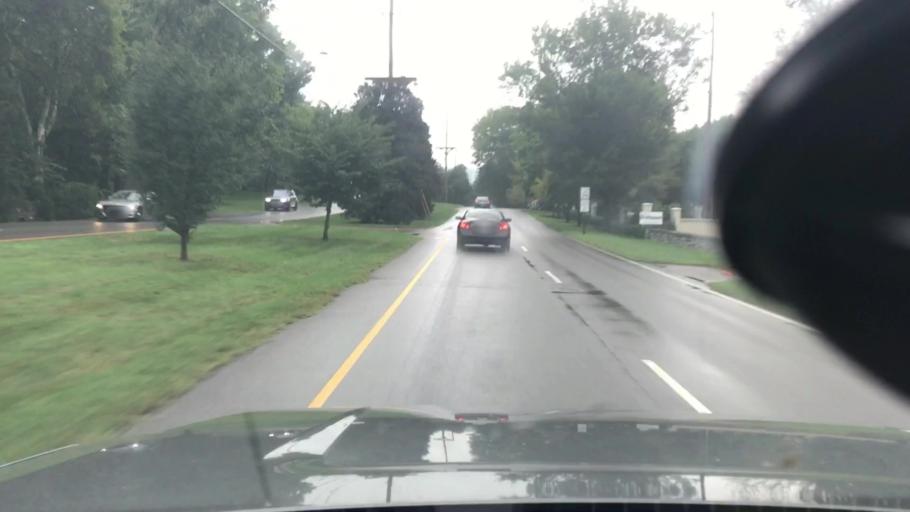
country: US
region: Tennessee
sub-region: Davidson County
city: Belle Meade
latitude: 36.1008
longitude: -86.8569
